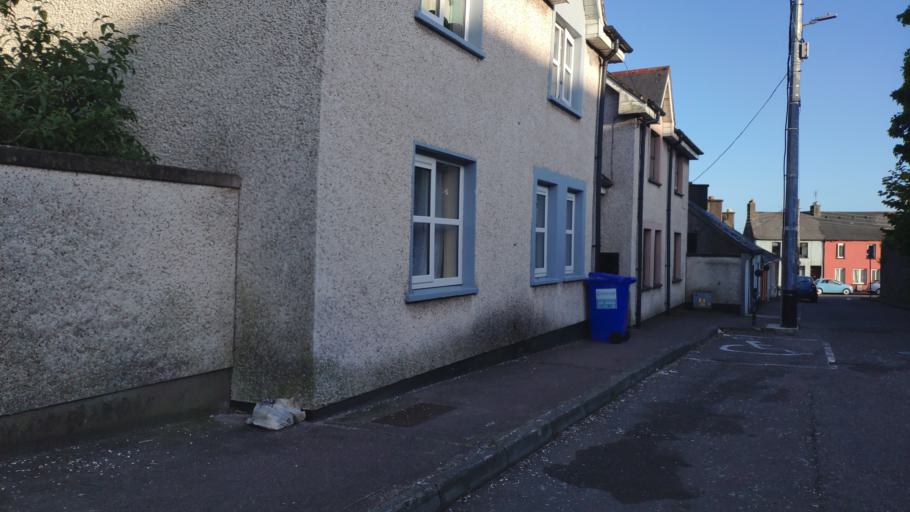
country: IE
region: Munster
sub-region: County Cork
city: Cork
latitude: 51.9078
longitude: -8.4605
